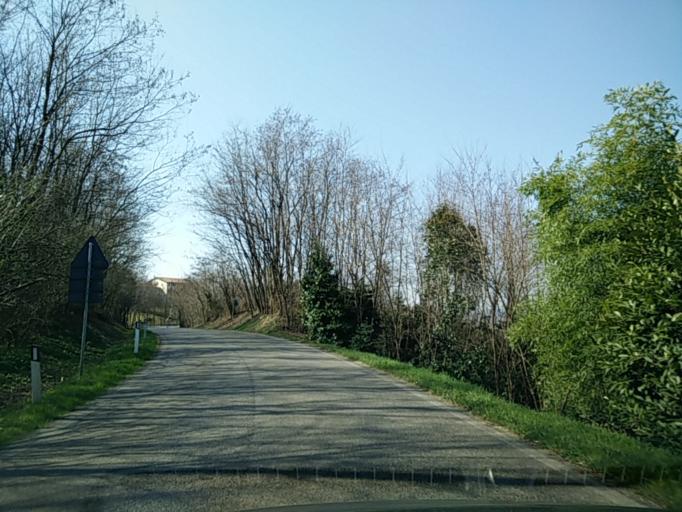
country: IT
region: Veneto
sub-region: Provincia di Treviso
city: Falze di Piave
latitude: 45.8476
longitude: 12.1551
